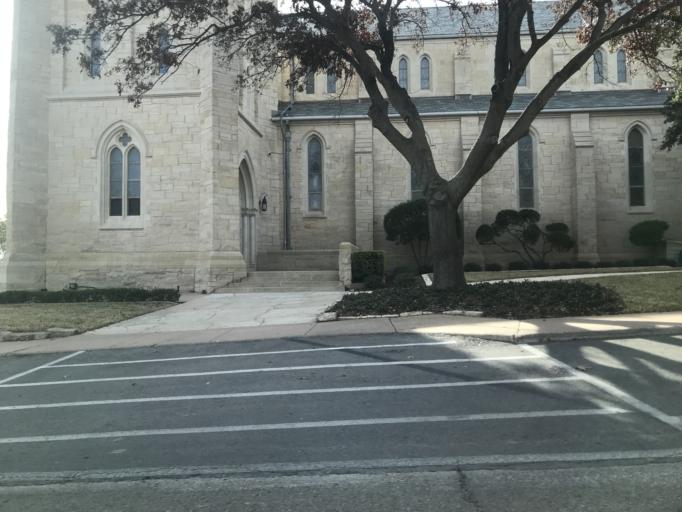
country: US
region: Texas
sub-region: Taylor County
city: Abilene
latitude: 32.4444
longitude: -99.7457
